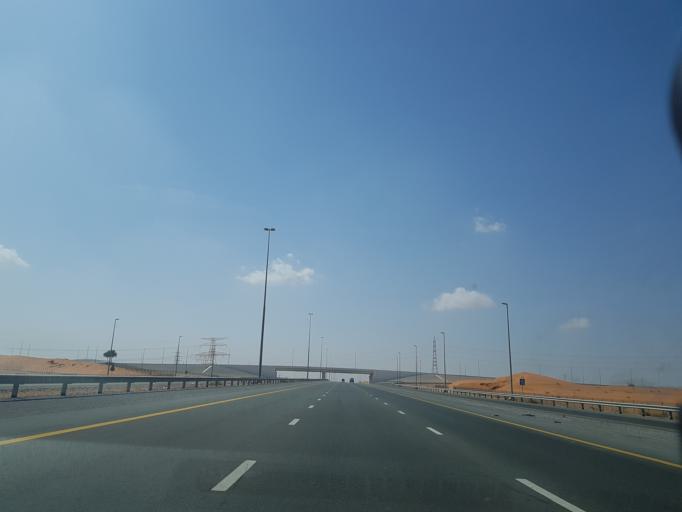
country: AE
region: Ra's al Khaymah
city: Ras al-Khaimah
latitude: 25.6975
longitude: 55.9280
